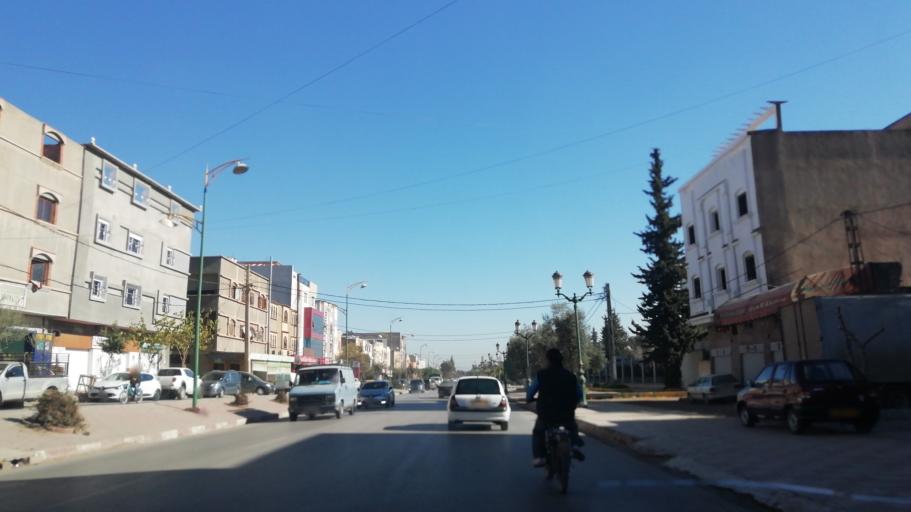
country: DZ
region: Tlemcen
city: Nedroma
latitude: 34.8451
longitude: -1.7474
